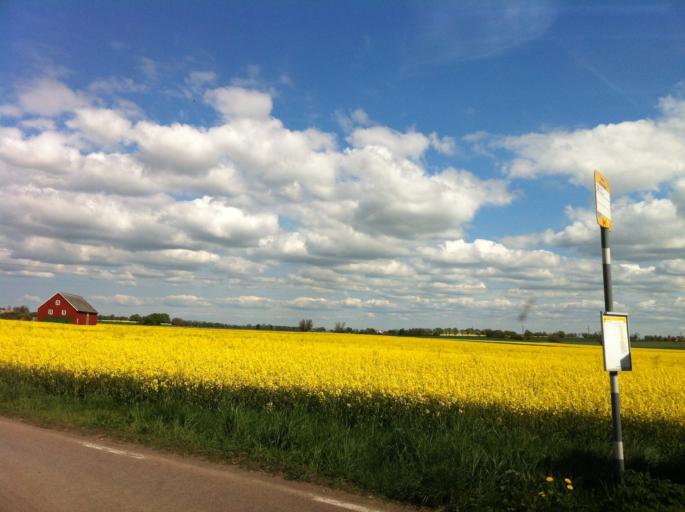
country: SE
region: Skane
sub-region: Helsingborg
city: Barslov
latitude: 55.9869
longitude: 12.8384
